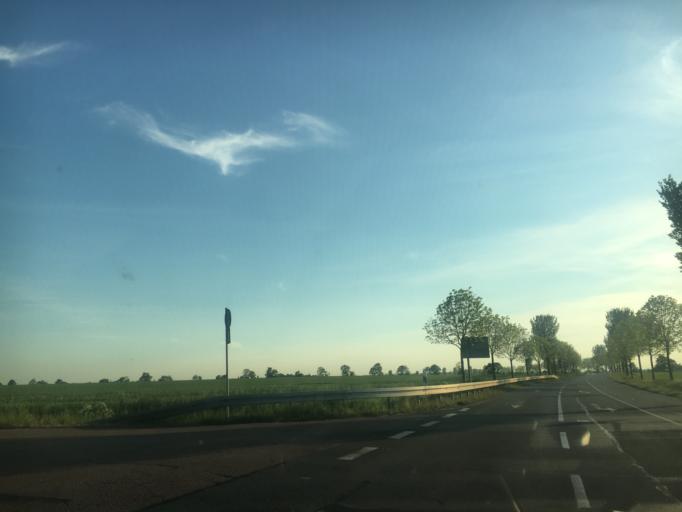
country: DE
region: Saxony-Anhalt
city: Loberitz
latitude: 51.6504
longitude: 12.1553
